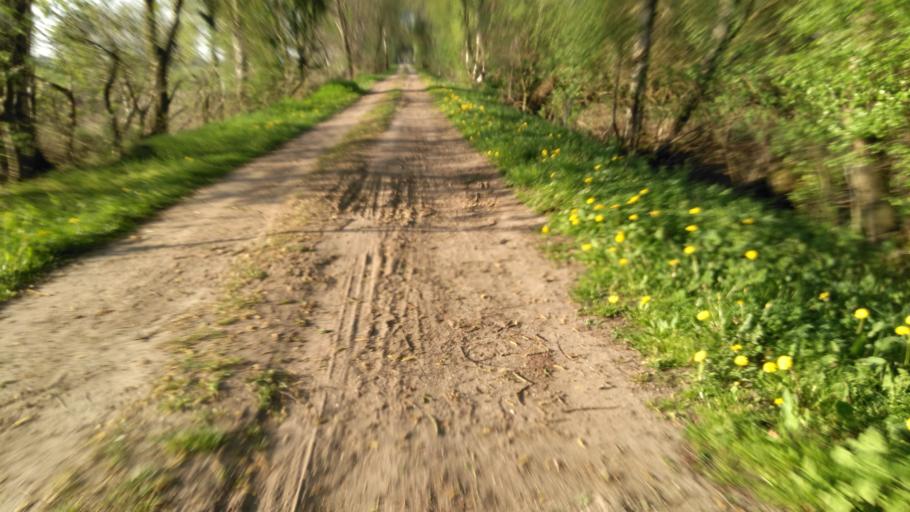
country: DE
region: Lower Saxony
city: Bliedersdorf
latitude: 53.4431
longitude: 9.5660
